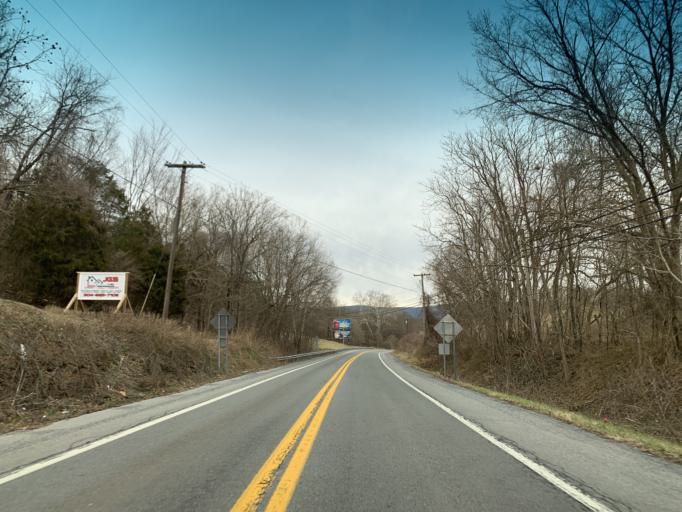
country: US
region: West Virginia
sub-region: Jefferson County
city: Charles Town
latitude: 39.2603
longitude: -77.8285
